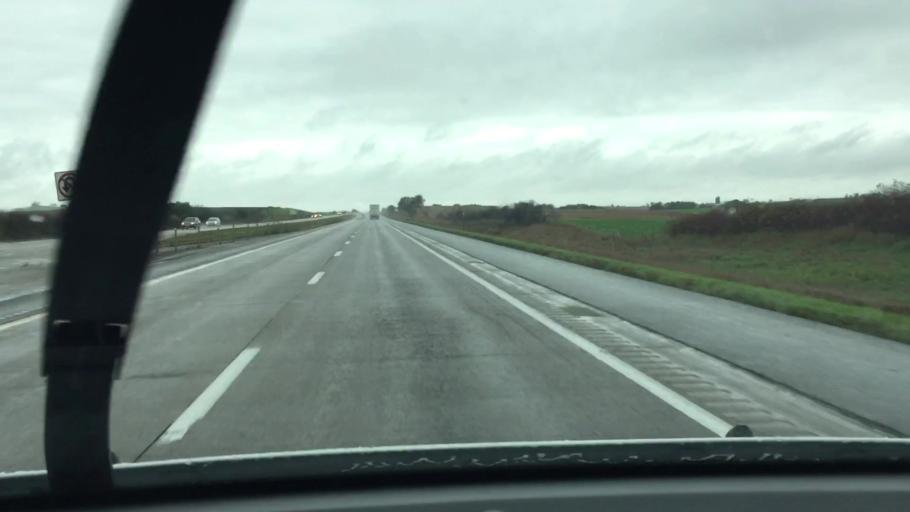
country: US
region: Iowa
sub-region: Poweshiek County
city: Brooklyn
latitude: 41.6952
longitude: -92.4639
